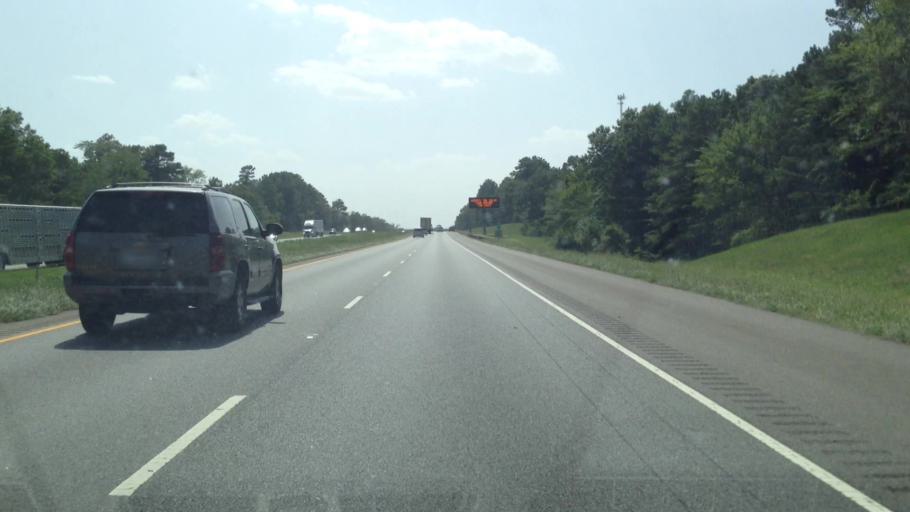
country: US
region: Louisiana
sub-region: Bossier Parish
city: Red Chute
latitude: 32.5421
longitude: -93.5923
